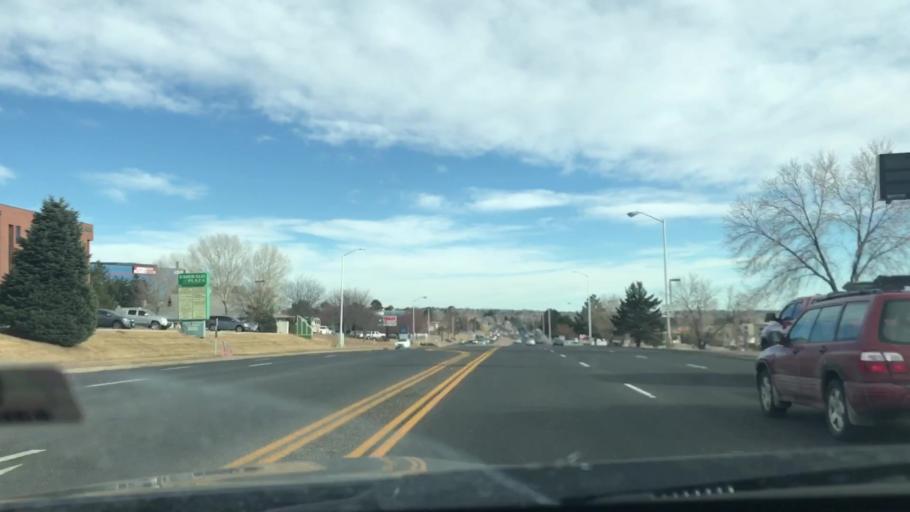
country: US
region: Colorado
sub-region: El Paso County
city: Colorado Springs
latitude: 38.9066
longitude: -104.7809
